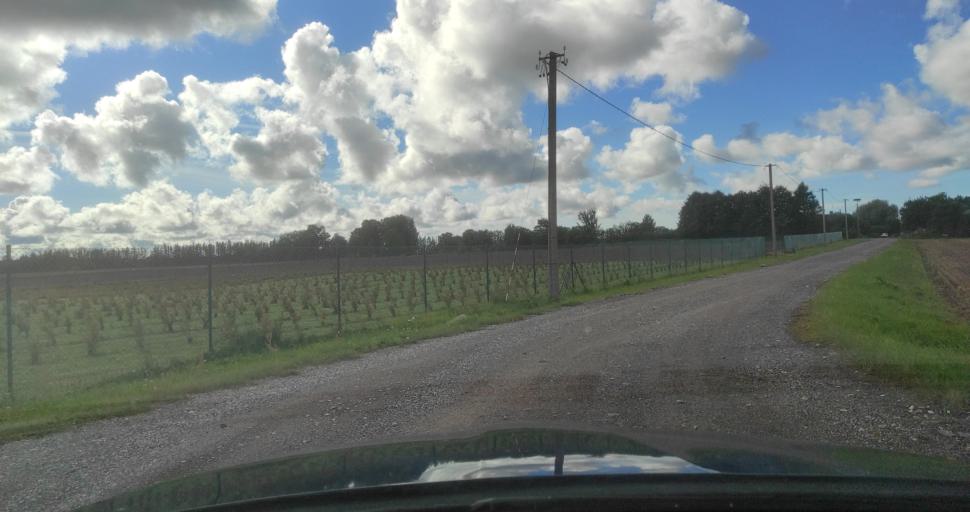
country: LV
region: Ventspils Rajons
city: Piltene
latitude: 57.2668
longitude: 21.6059
